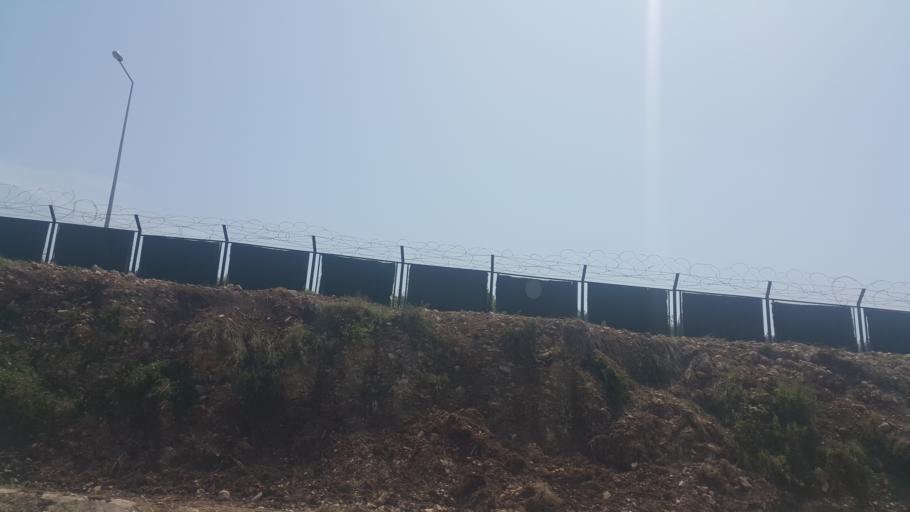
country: TR
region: Hatay
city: Denizciler
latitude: 36.6326
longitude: 36.2027
